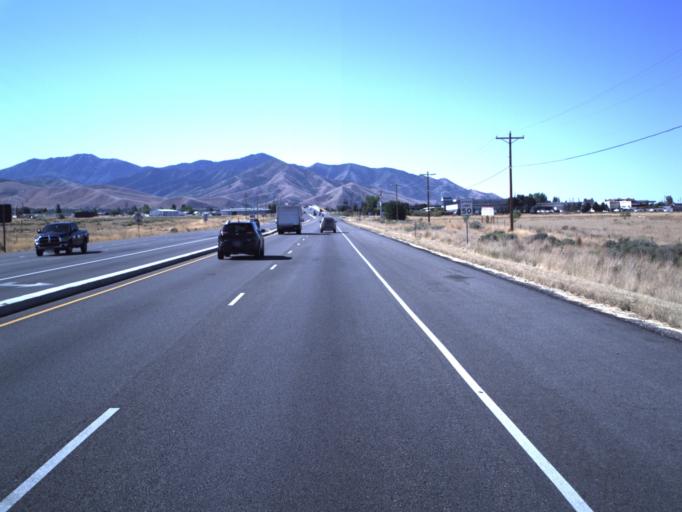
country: US
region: Utah
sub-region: Tooele County
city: Tooele
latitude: 40.5721
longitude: -112.2952
